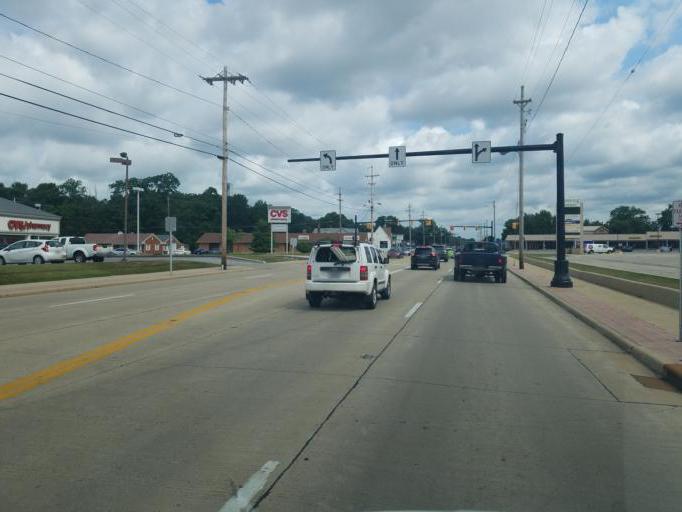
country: US
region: Ohio
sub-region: Lake County
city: Painesville
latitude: 41.6998
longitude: -81.2768
